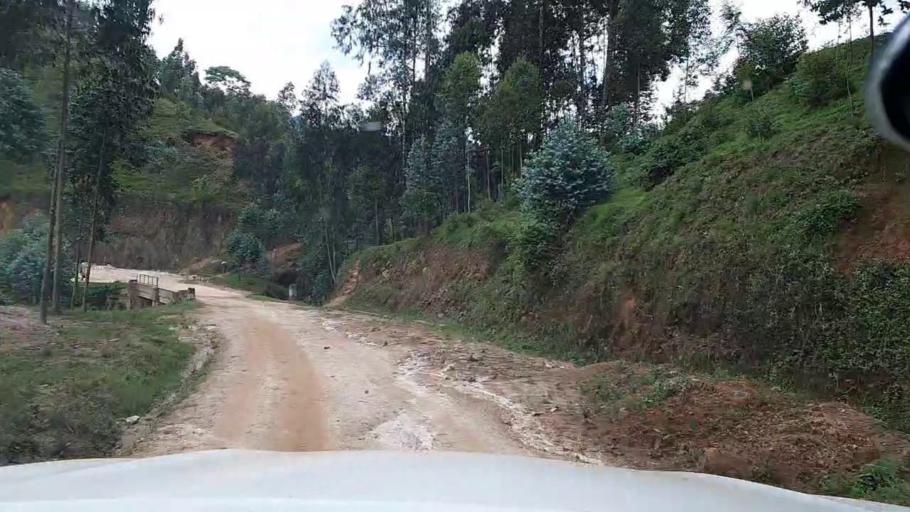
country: RW
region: Southern Province
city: Nzega
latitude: -2.6988
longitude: 29.4381
